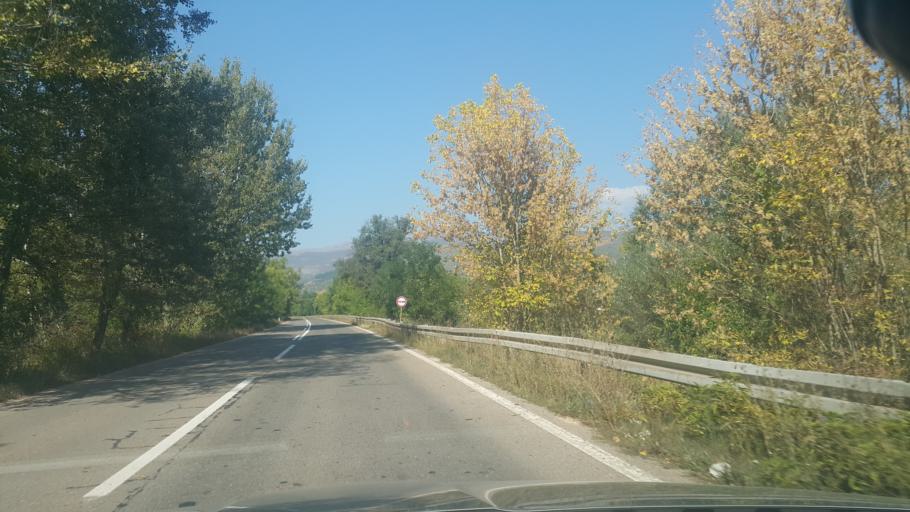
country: RS
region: Central Serbia
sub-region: Pirotski Okrug
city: Bela Palanka
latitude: 43.2497
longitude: 22.2641
